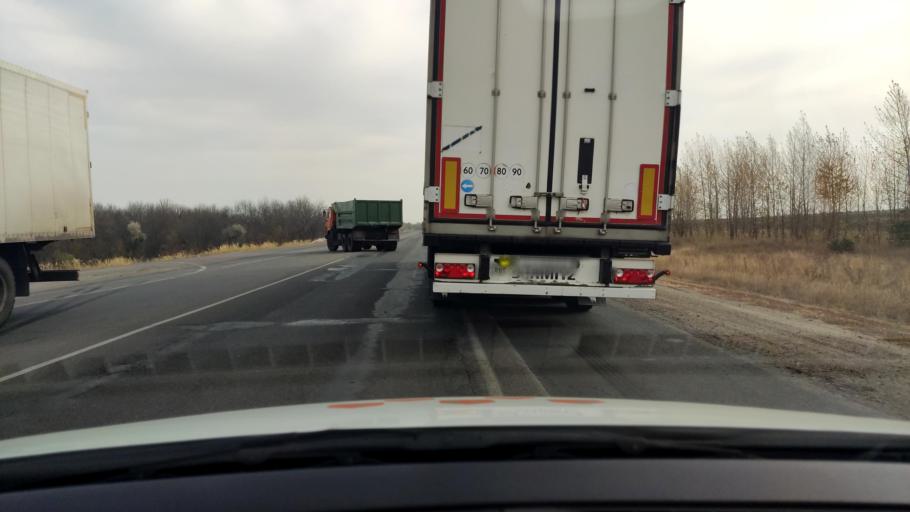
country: RU
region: Voronezj
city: Somovo
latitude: 51.6982
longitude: 39.4012
